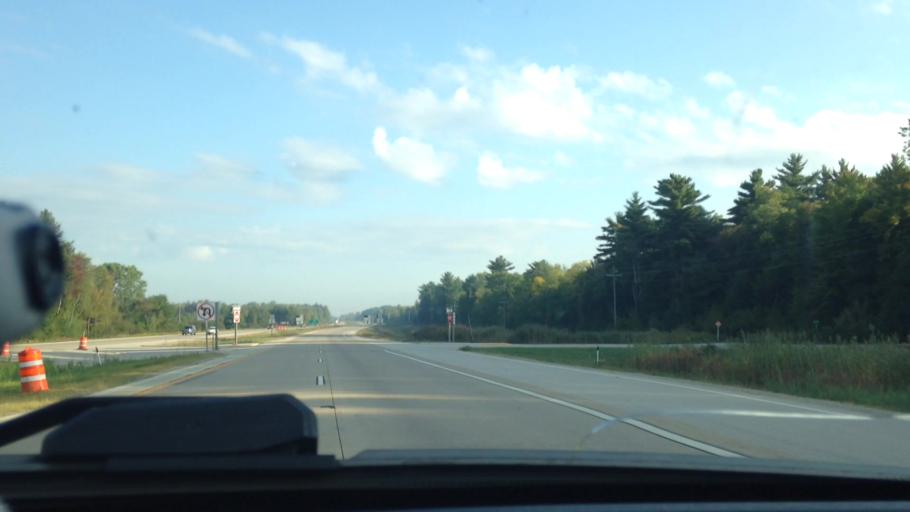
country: US
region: Wisconsin
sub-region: Oconto County
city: Oconto Falls
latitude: 44.7984
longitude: -88.0495
